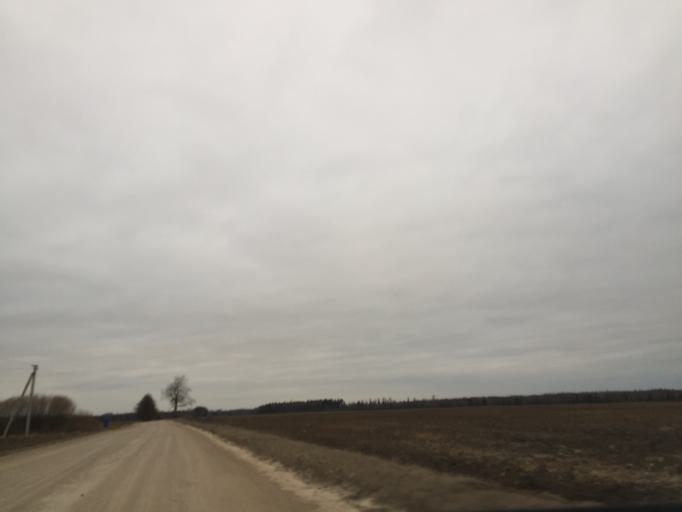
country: LT
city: Zagare
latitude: 56.2733
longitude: 23.2624
